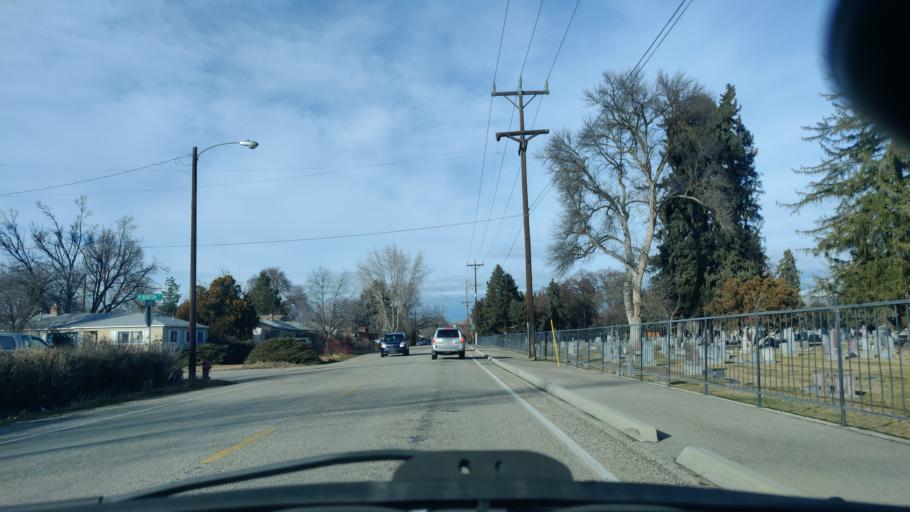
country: US
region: Idaho
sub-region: Ada County
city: Garden City
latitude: 43.6094
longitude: -116.2335
